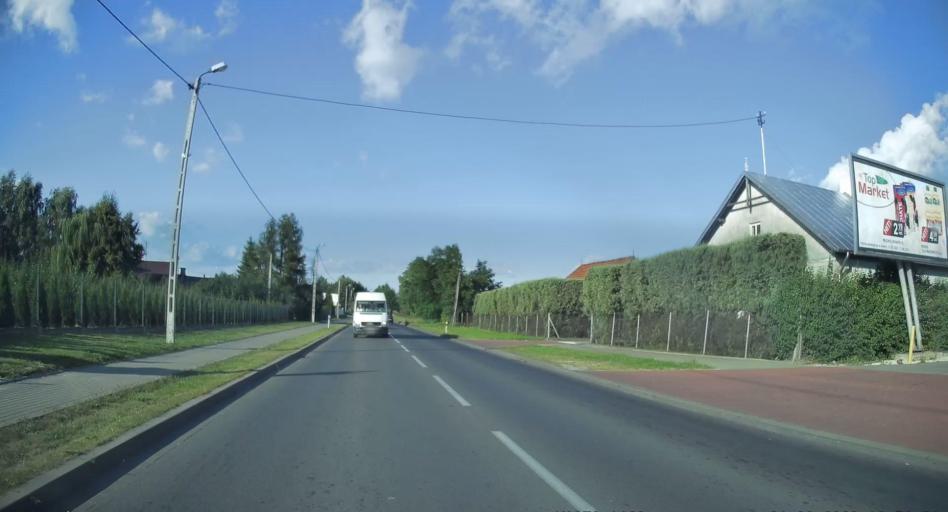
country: PL
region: Masovian Voivodeship
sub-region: Powiat grojecki
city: Belsk Duzy
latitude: 51.8265
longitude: 20.8103
